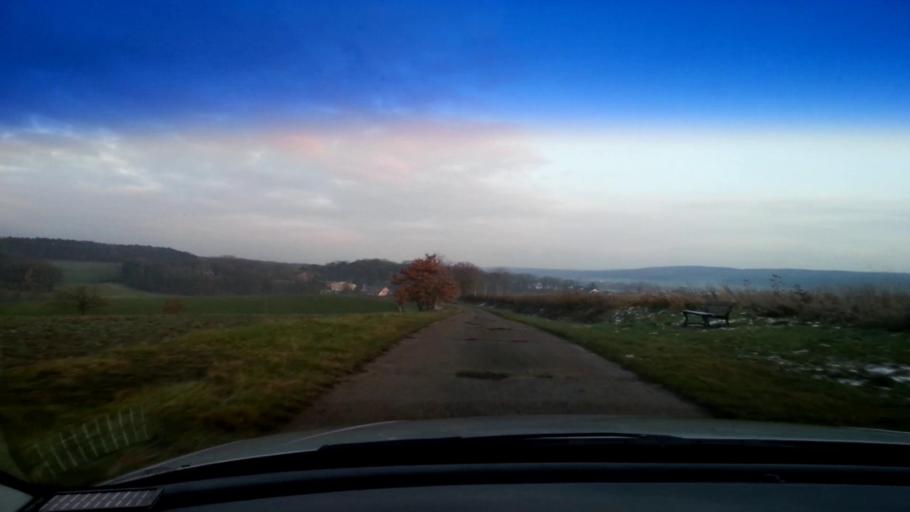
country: DE
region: Bavaria
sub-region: Upper Franconia
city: Frensdorf
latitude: 49.7888
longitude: 10.8522
